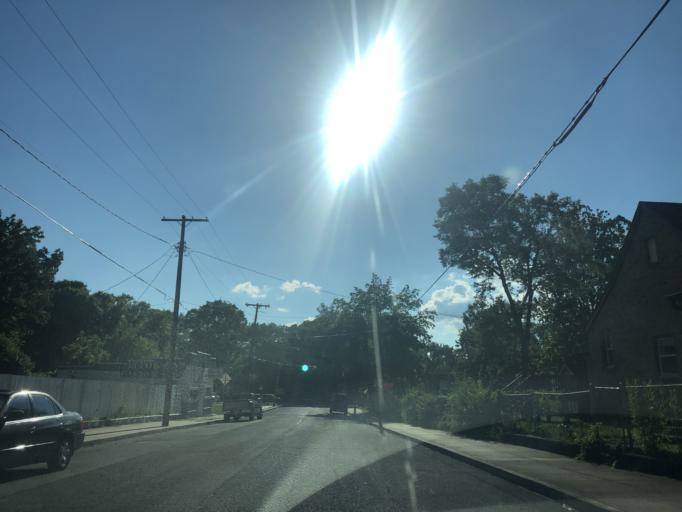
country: US
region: Tennessee
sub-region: Davidson County
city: Nashville
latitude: 36.1884
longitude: -86.7628
